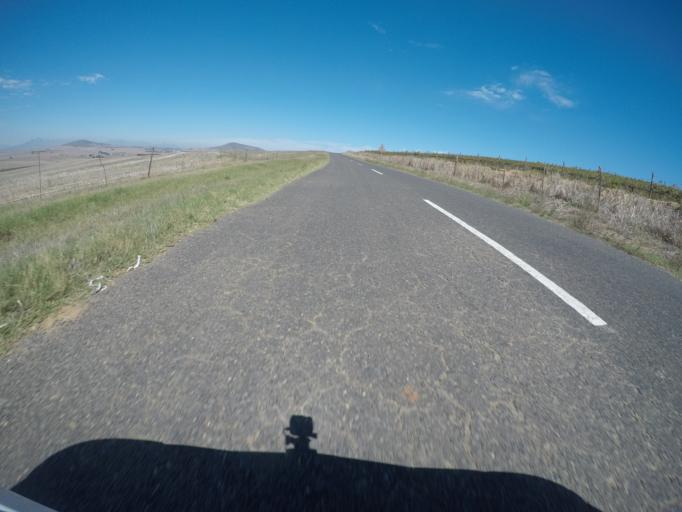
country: ZA
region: Western Cape
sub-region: City of Cape Town
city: Sunset Beach
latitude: -33.7124
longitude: 18.5822
